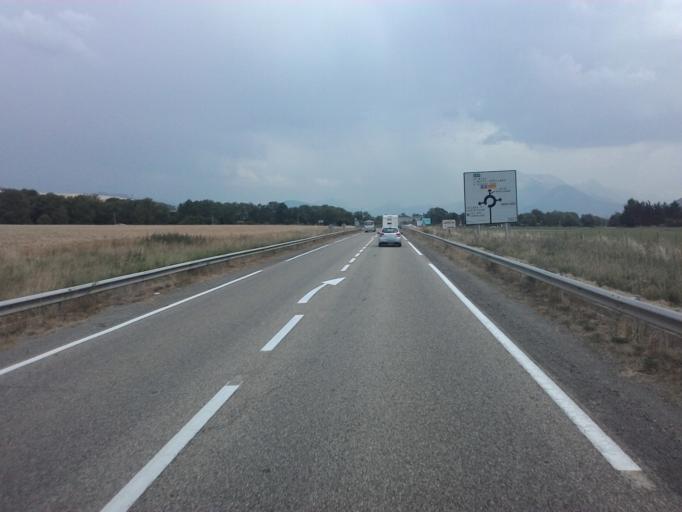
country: FR
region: Rhone-Alpes
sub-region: Departement de l'Isere
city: Pierre-Chatel
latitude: 44.9619
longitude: 5.7789
